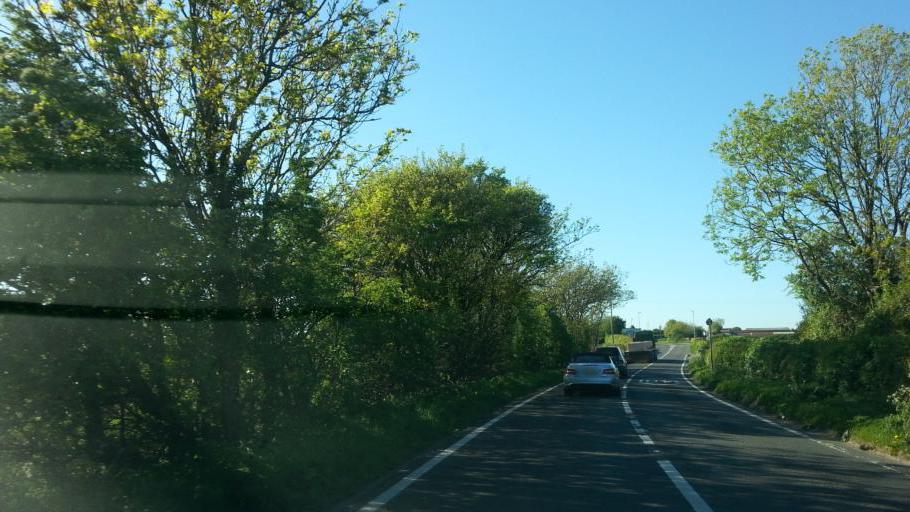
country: GB
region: England
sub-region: Somerset
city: Shepton Mallet
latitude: 51.1678
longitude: -2.5331
